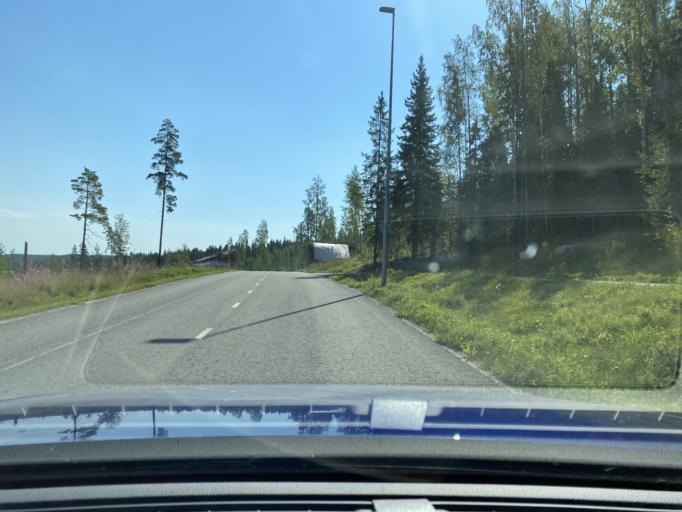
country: FI
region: Central Finland
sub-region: Jaemsae
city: Jaemsae
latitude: 61.8906
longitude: 25.3883
